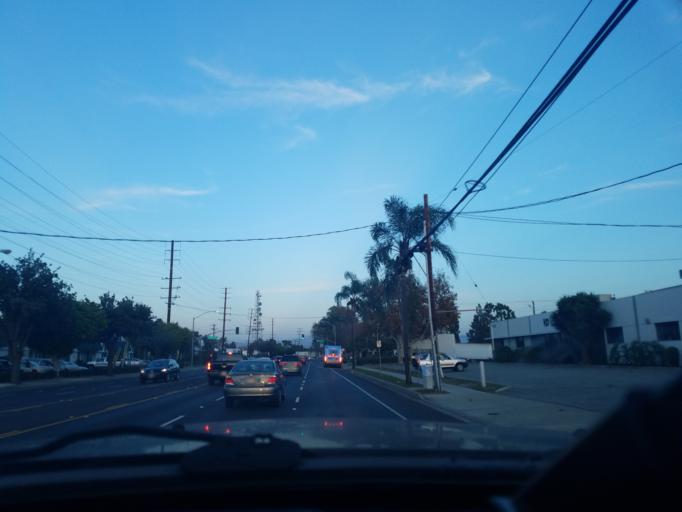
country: US
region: California
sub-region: Orange County
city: Fountain Valley
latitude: 33.7141
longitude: -117.9140
